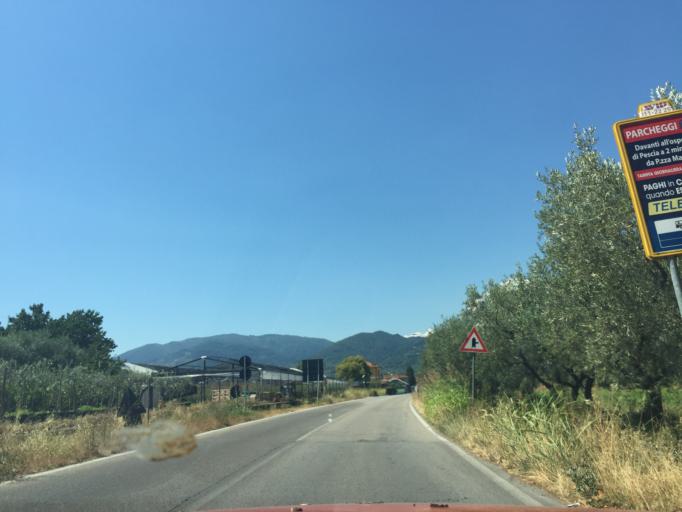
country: IT
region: Tuscany
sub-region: Provincia di Pistoia
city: Pescia
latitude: 43.8737
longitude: 10.6922
